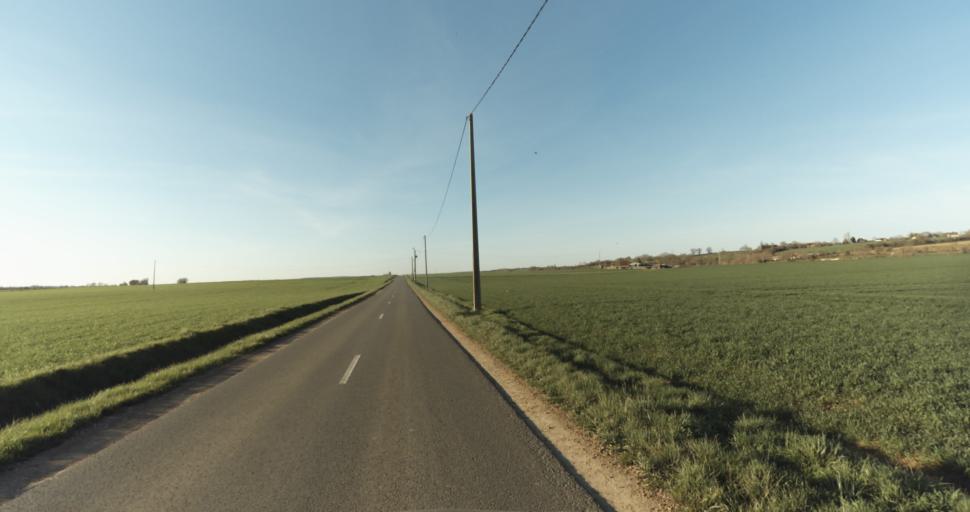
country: FR
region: Lower Normandy
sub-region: Departement du Calvados
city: Saint-Pierre-sur-Dives
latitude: 48.9988
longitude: -0.0217
